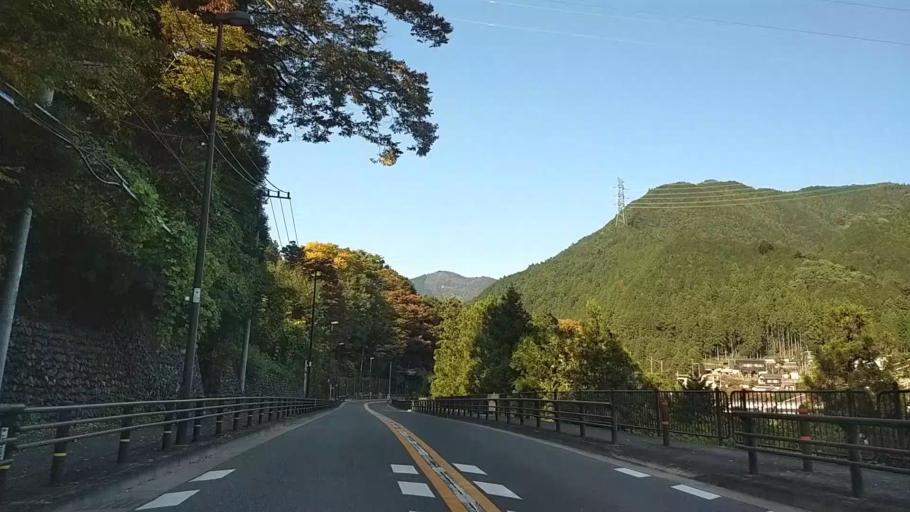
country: JP
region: Tokyo
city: Ome
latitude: 35.8109
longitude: 139.1620
